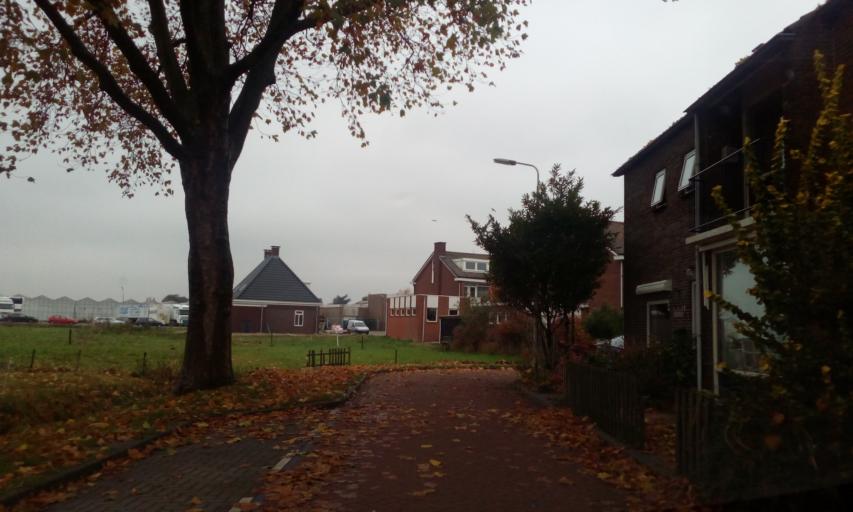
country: NL
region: South Holland
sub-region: Gemeente Lansingerland
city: Berkel en Rodenrijs
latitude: 51.9741
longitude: 4.4566
